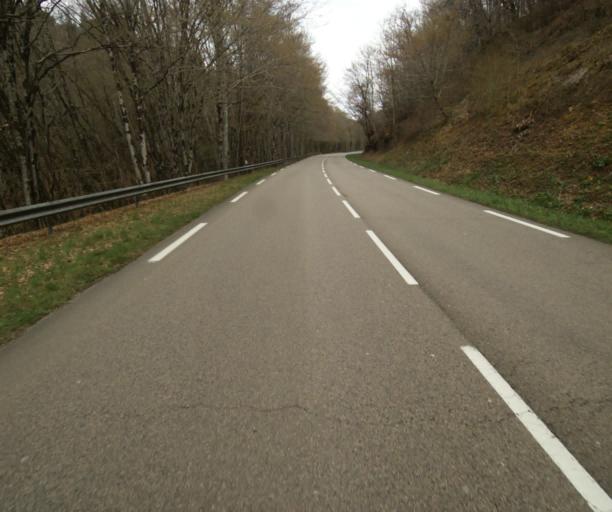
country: FR
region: Limousin
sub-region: Departement de la Correze
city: Sainte-Fortunade
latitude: 45.1872
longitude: 1.8465
